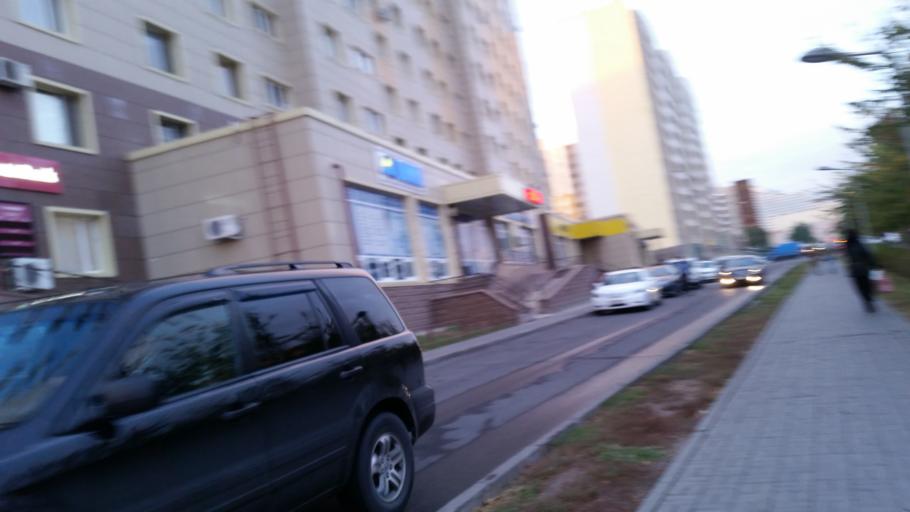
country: KZ
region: Astana Qalasy
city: Astana
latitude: 51.1218
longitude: 71.4209
